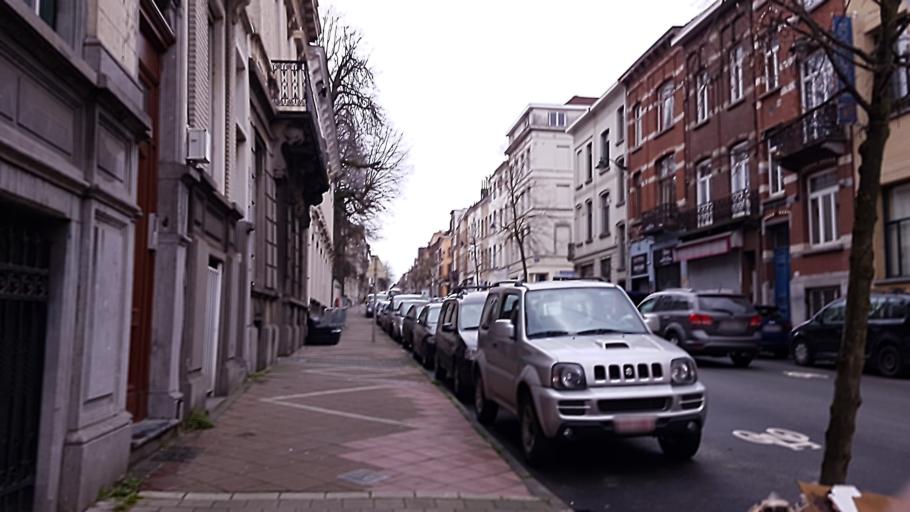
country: BE
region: Brussels Capital
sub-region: Bruxelles-Capitale
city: Brussels
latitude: 50.8346
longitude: 4.3841
